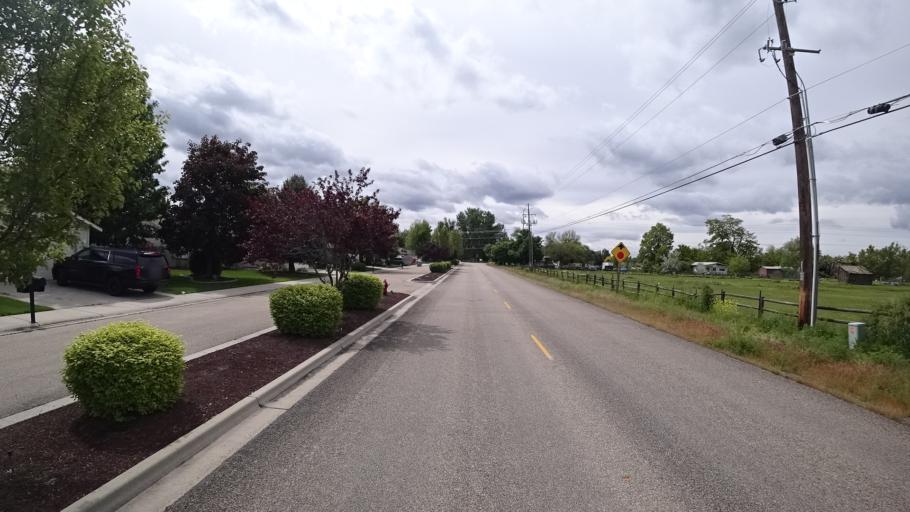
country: US
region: Idaho
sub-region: Ada County
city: Eagle
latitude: 43.6797
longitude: -116.3015
